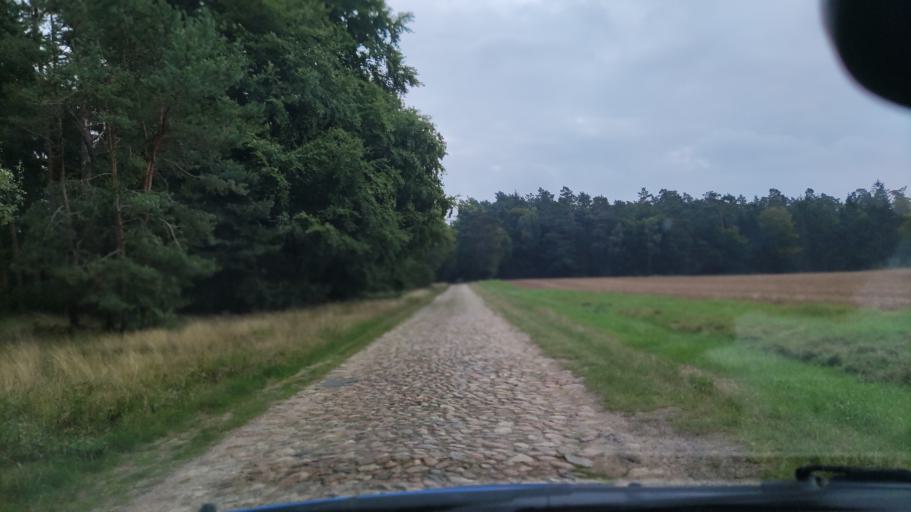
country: DE
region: Lower Saxony
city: Altenmedingen
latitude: 53.1540
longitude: 10.5770
